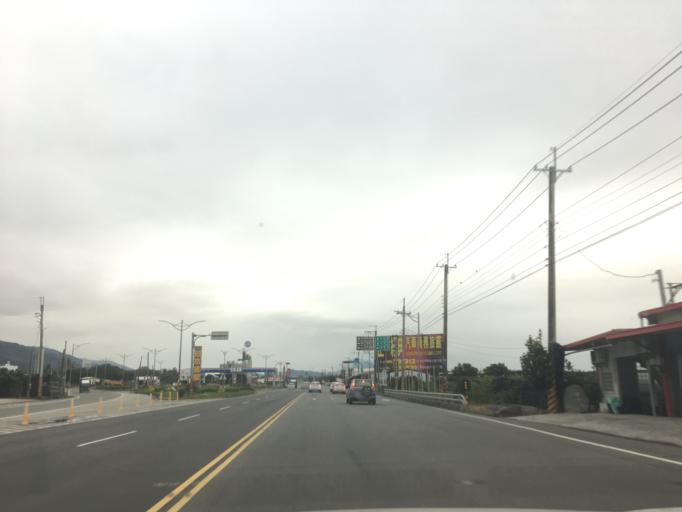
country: TW
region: Taiwan
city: Taitung City
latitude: 22.6894
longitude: 121.0462
